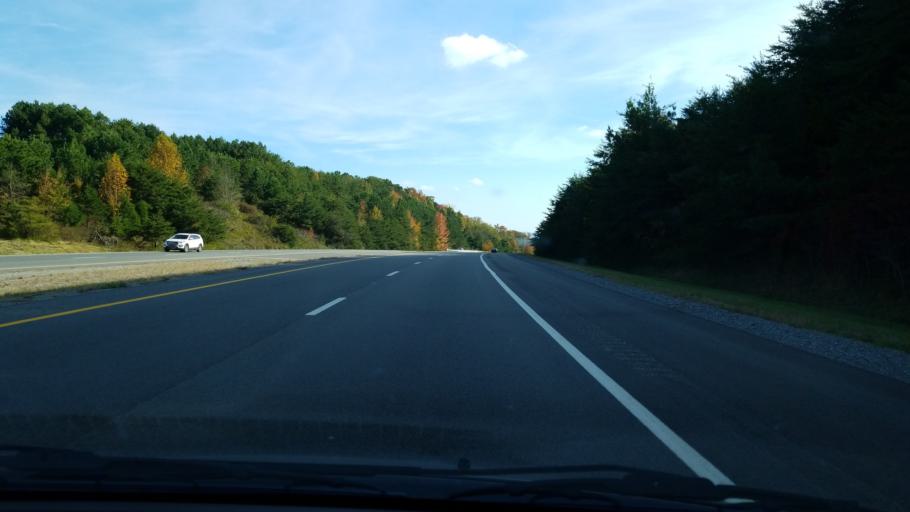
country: US
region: Tennessee
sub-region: Hamilton County
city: Sale Creek
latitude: 35.3401
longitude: -85.1683
